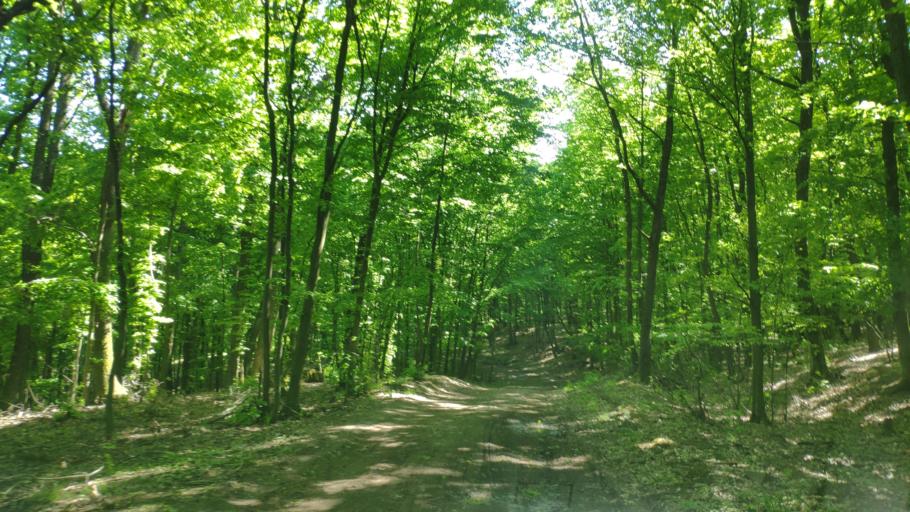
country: SK
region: Kosicky
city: Secovce
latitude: 48.7092
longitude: 21.5830
